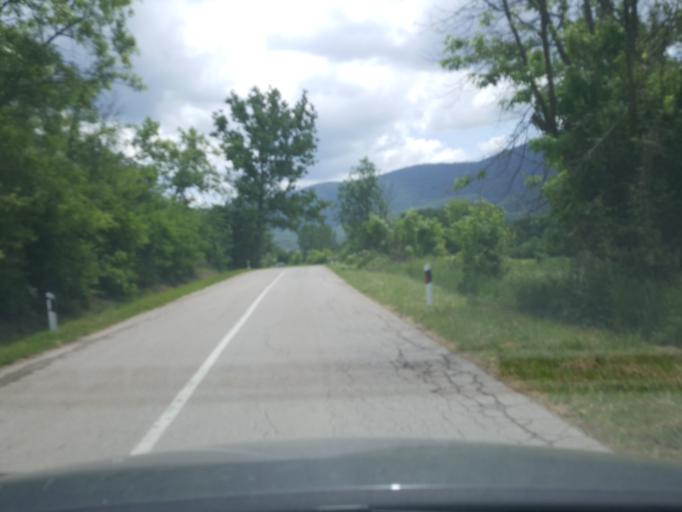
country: RS
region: Central Serbia
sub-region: Zajecarski Okrug
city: Soko Banja
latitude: 43.6458
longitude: 21.9331
